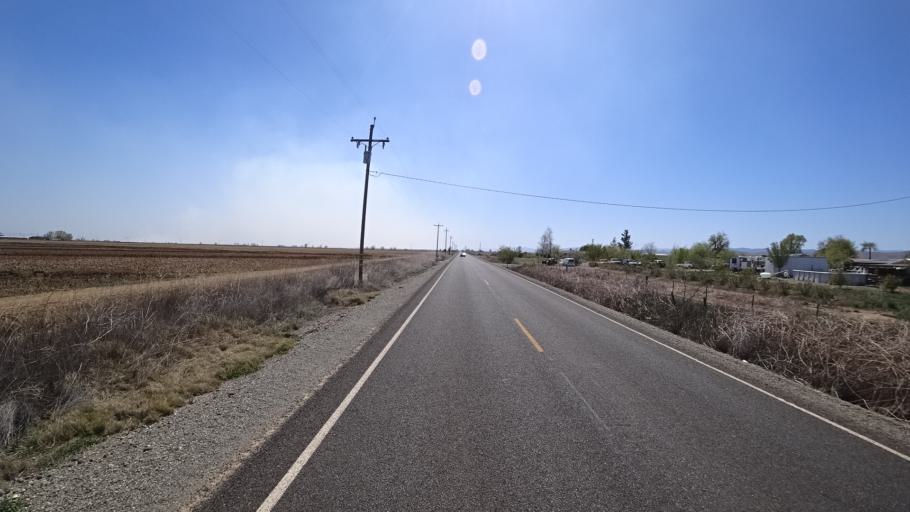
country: US
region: California
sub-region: Glenn County
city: Willows
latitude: 39.4119
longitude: -122.2485
